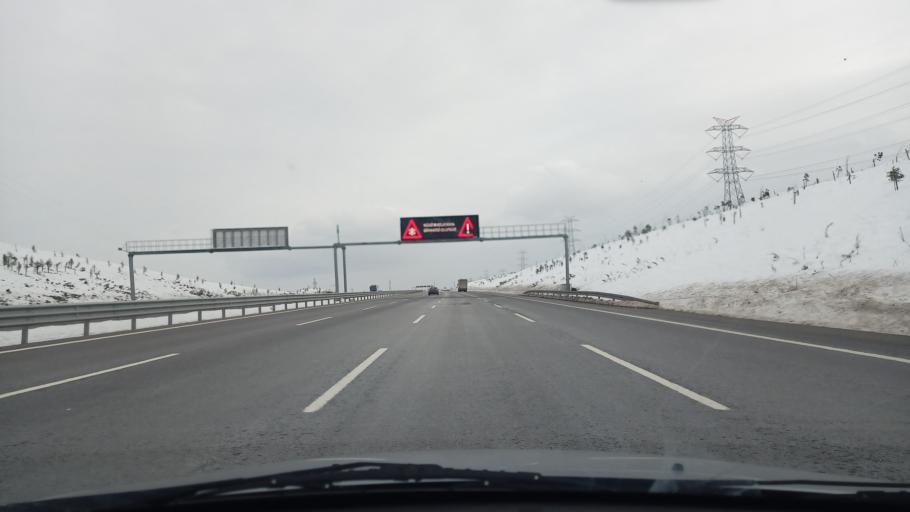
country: TR
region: Kocaeli
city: Korfez
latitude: 40.8673
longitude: 29.7905
